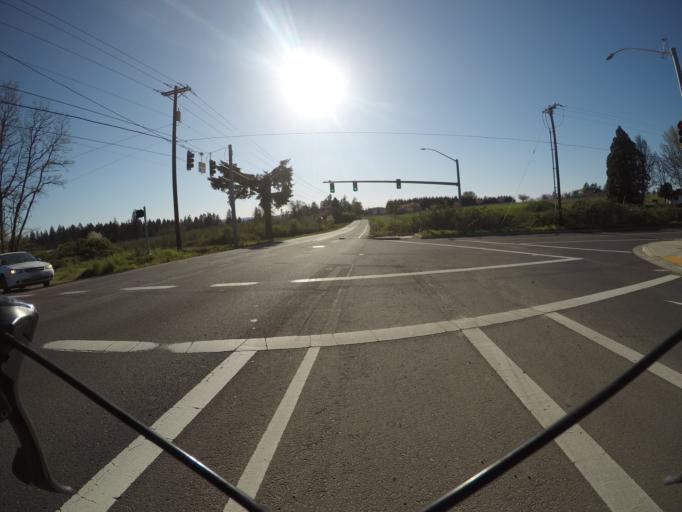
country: US
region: Oregon
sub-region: Washington County
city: King City
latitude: 45.4259
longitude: -122.8597
